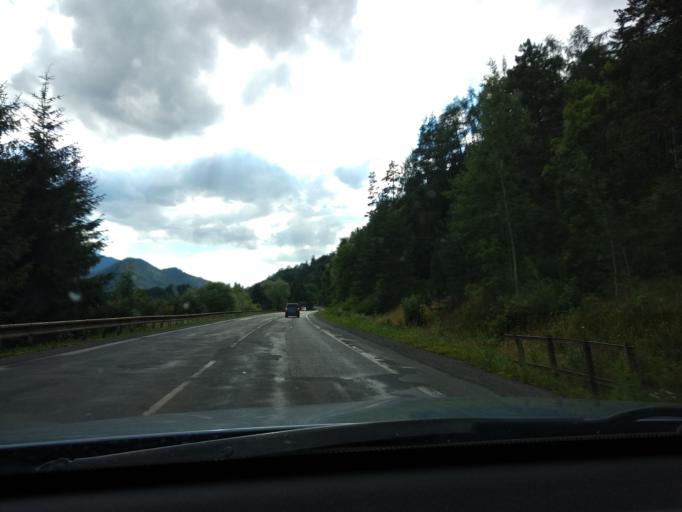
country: SK
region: Zilinsky
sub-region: Okres Zilina
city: Liptovsky Hradok
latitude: 49.0384
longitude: 19.7425
